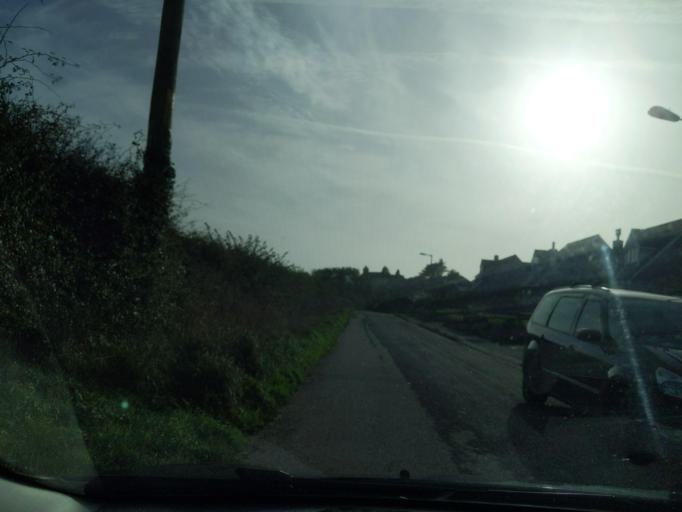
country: GB
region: England
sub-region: Cornwall
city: Pillaton
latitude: 50.3676
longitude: -4.2984
